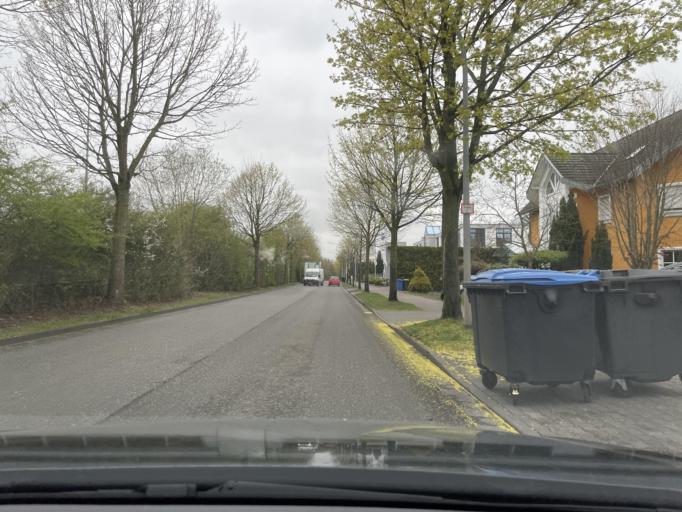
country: DE
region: North Rhine-Westphalia
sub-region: Regierungsbezirk Dusseldorf
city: Monchengladbach
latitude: 51.1212
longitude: 6.4372
